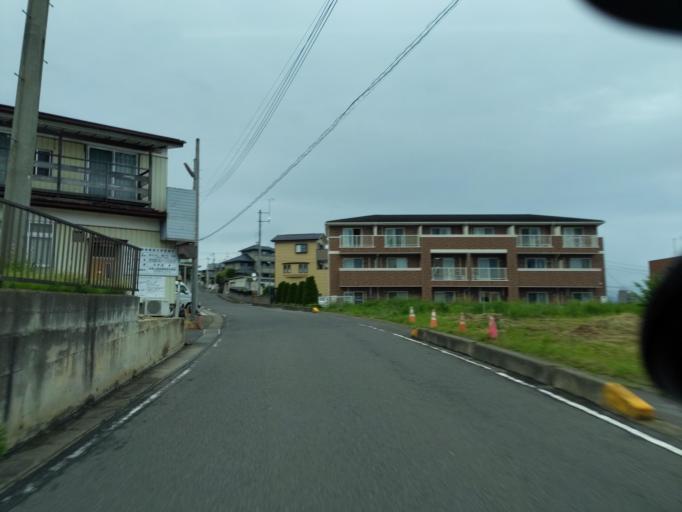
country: JP
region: Fukushima
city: Koriyama
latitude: 37.3608
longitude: 140.3585
